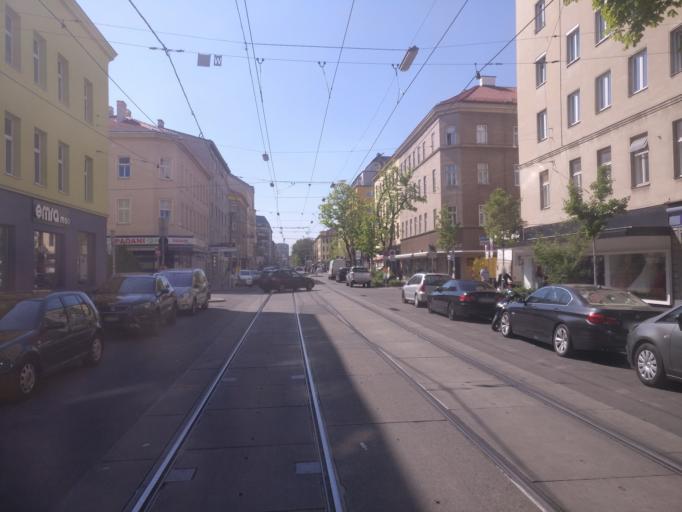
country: AT
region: Vienna
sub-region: Wien Stadt
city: Vienna
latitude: 48.1754
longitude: 16.3760
